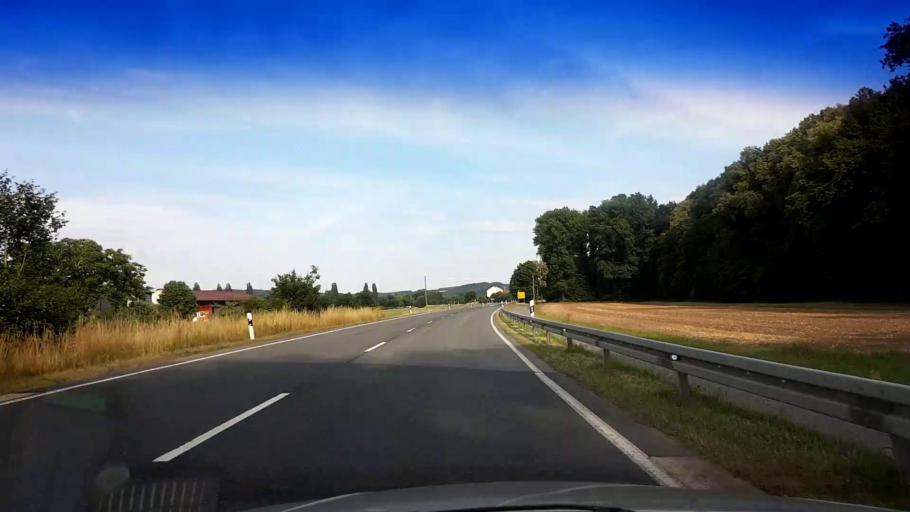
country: DE
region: Bavaria
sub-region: Regierungsbezirk Unterfranken
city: Eltmann
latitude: 49.9688
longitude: 10.6895
